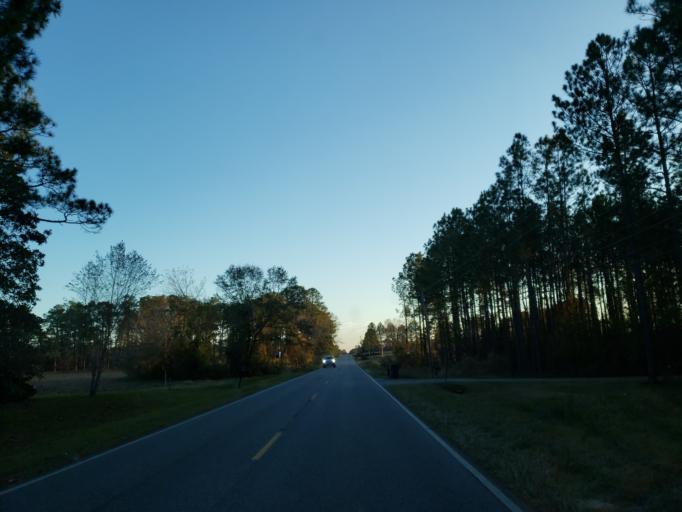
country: US
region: Georgia
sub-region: Crisp County
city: Cordele
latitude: 31.9463
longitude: -83.7658
